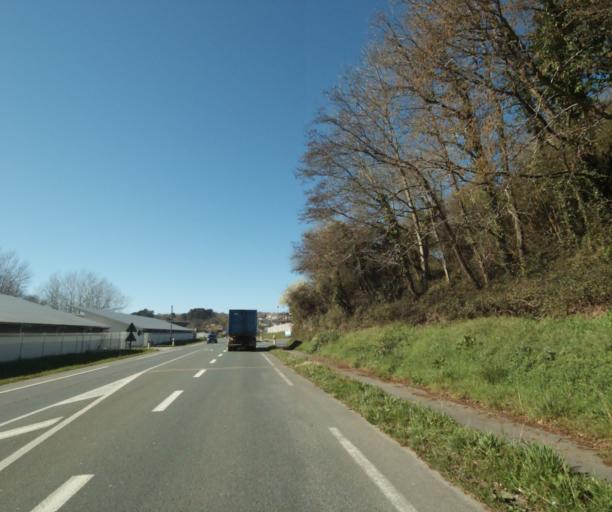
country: FR
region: Aquitaine
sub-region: Departement des Pyrenees-Atlantiques
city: Ciboure
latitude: 43.3819
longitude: -1.6903
